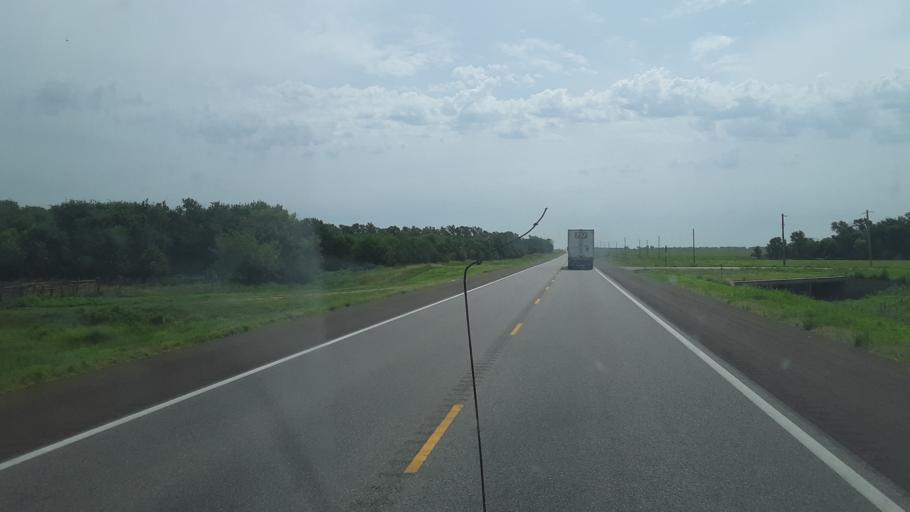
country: US
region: Kansas
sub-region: Reno County
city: Nickerson
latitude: 37.9849
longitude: -98.1434
